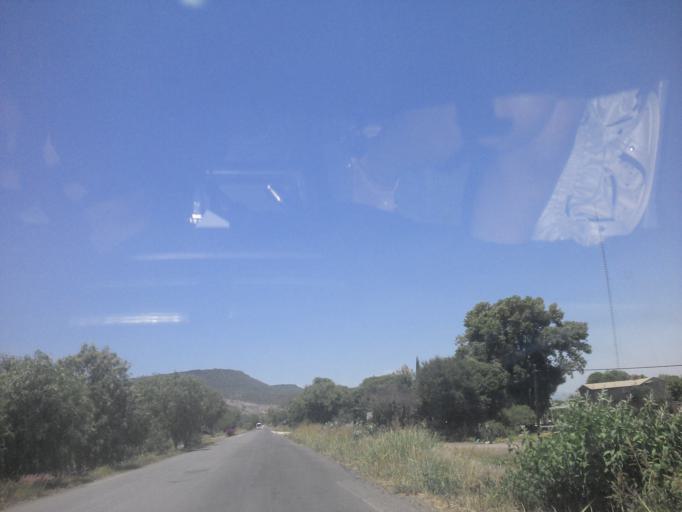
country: MX
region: Guanajuato
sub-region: San Francisco del Rincon
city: San Ignacio de Hidalgo
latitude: 20.9189
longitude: -101.9172
